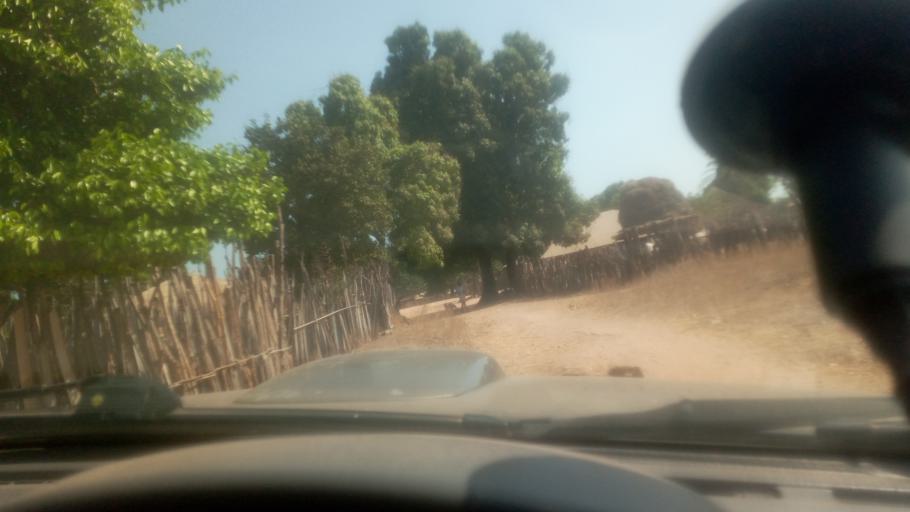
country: GW
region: Oio
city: Farim
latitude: 12.4614
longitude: -15.4072
